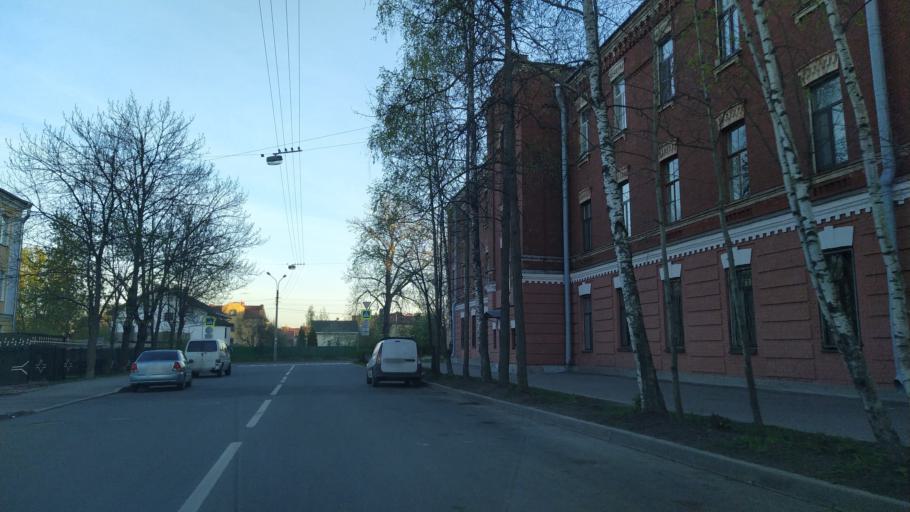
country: RU
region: St.-Petersburg
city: Pushkin
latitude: 59.7040
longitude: 30.4114
